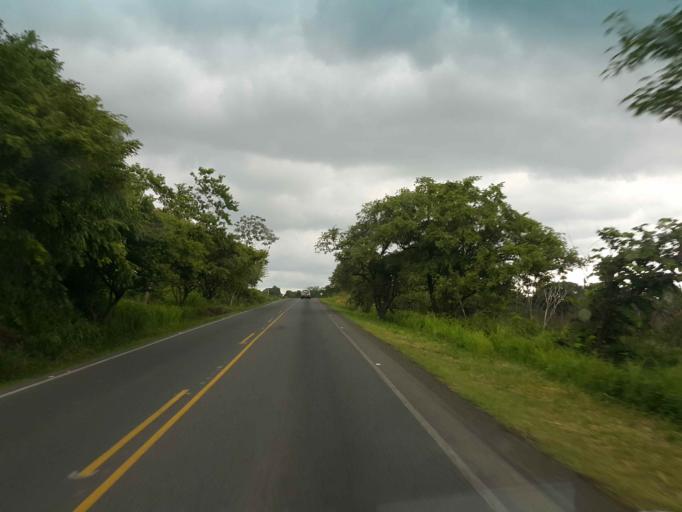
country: CR
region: Puntarenas
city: Miramar
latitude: 10.0990
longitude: -84.8040
